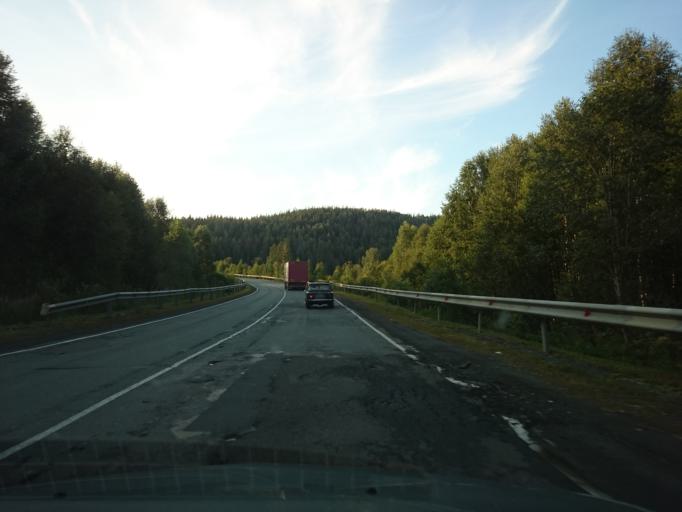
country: RU
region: Bashkortostan
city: Inzer
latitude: 53.9697
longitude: 57.8757
